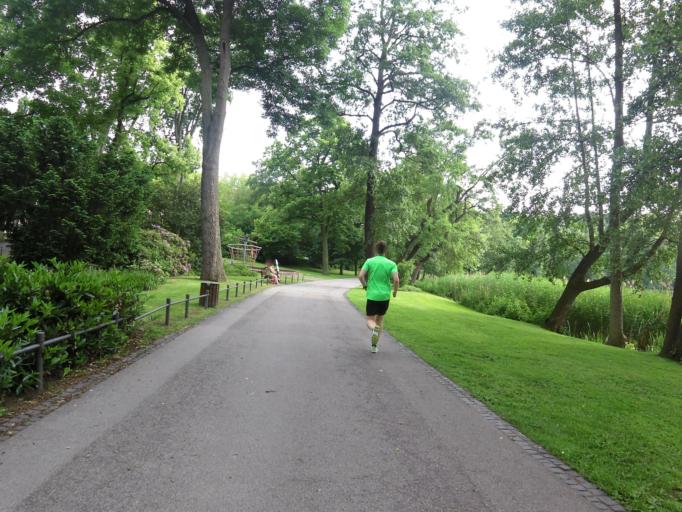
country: DE
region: Thuringia
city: Bad Salzungen
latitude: 50.8100
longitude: 10.2396
